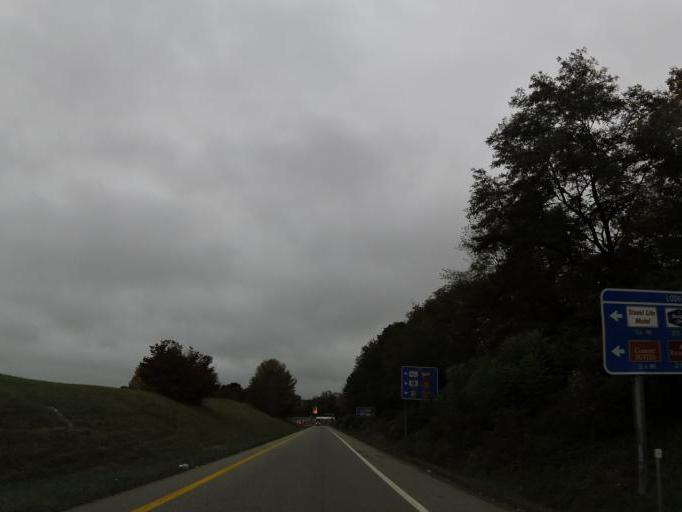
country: US
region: Virginia
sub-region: Wythe County
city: Wytheville
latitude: 36.9613
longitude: -81.0968
